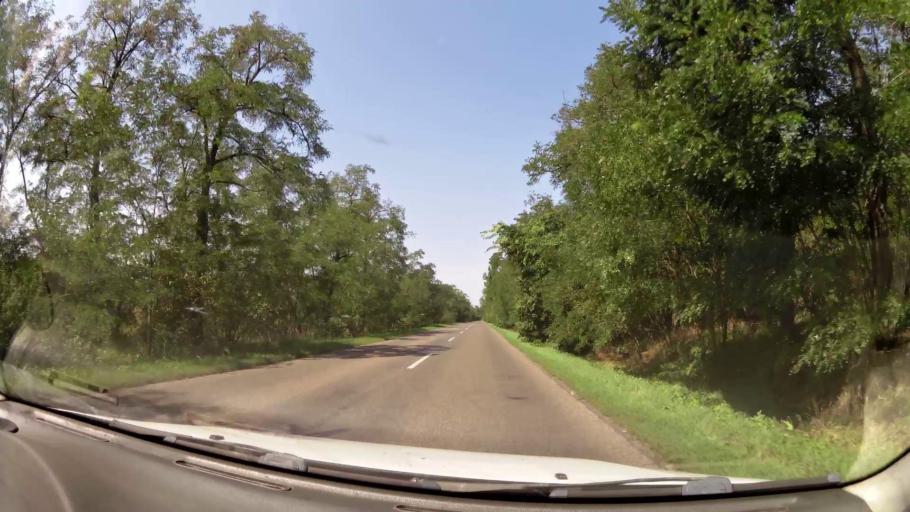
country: HU
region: Pest
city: Tapiosag
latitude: 47.3890
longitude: 19.6472
